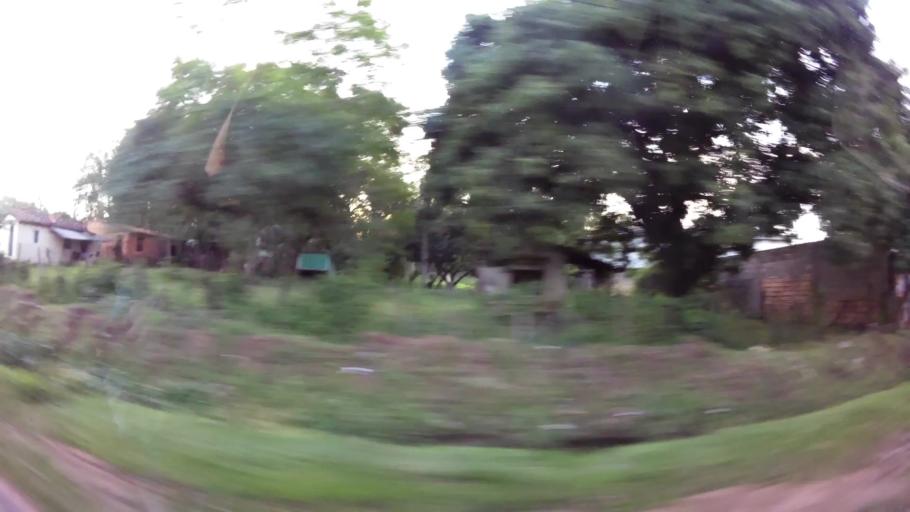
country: PY
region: Central
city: San Lorenzo
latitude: -25.3540
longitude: -57.4908
